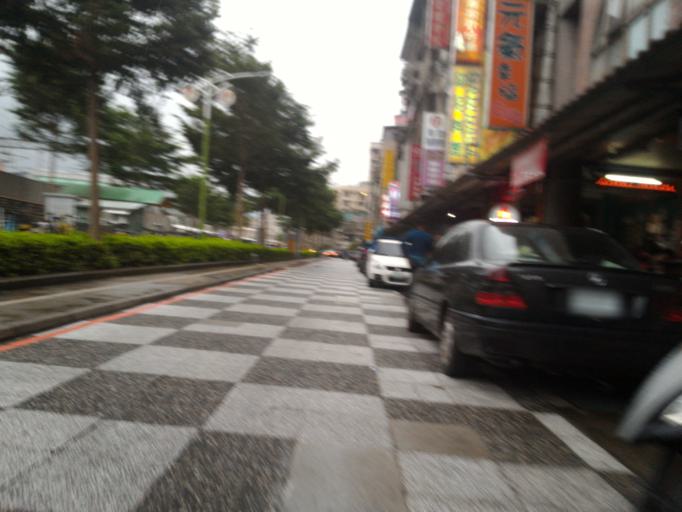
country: TW
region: Taipei
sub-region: Taipei
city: Banqiao
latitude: 24.9910
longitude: 121.4237
